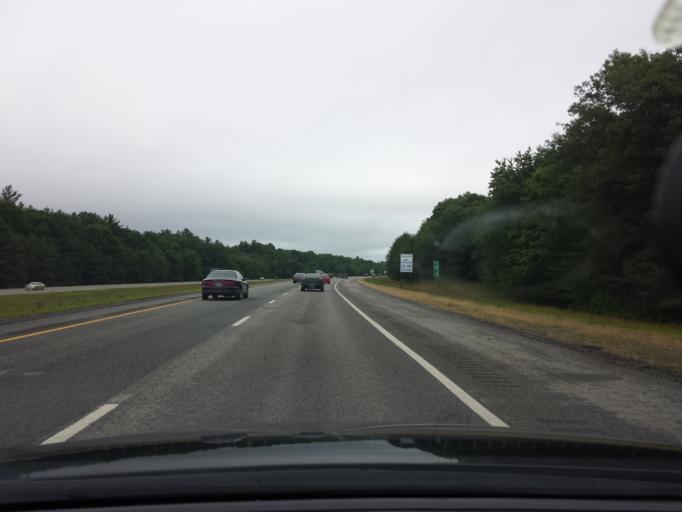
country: US
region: Rhode Island
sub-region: Kent County
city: West Greenwich
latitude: 41.6102
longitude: -71.6540
